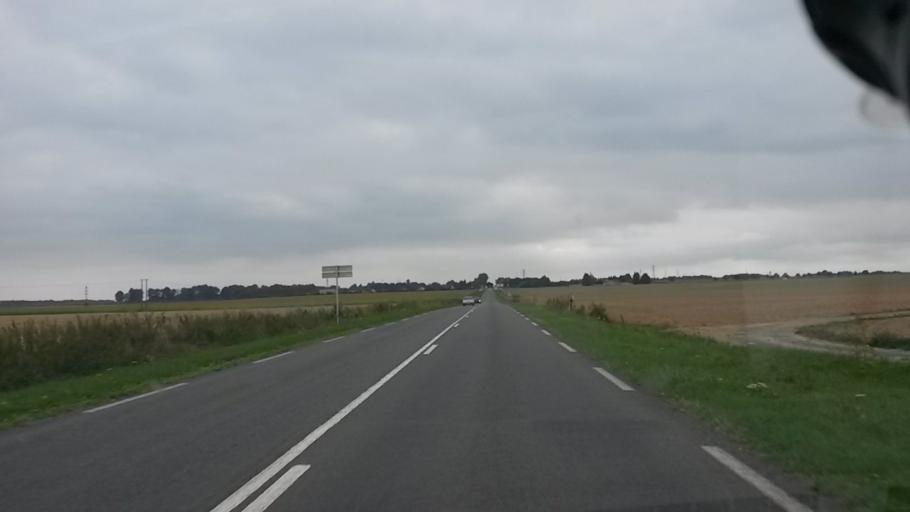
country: FR
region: Haute-Normandie
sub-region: Departement de la Seine-Maritime
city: Aumale
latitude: 49.7692
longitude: 1.8164
